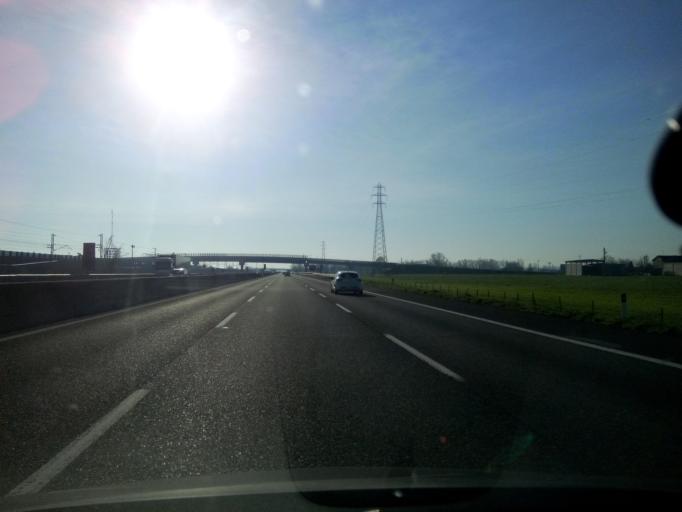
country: IT
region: Emilia-Romagna
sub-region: Provincia di Reggio Emilia
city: Prato
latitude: 44.6972
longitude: 10.7589
